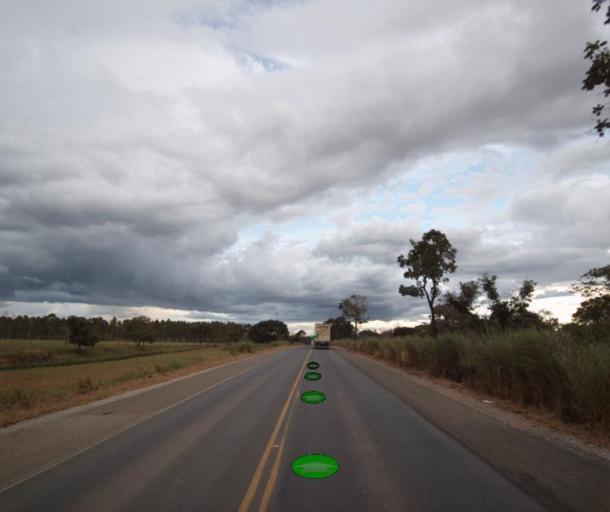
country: BR
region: Goias
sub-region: Uruacu
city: Uruacu
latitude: -14.7919
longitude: -49.2794
